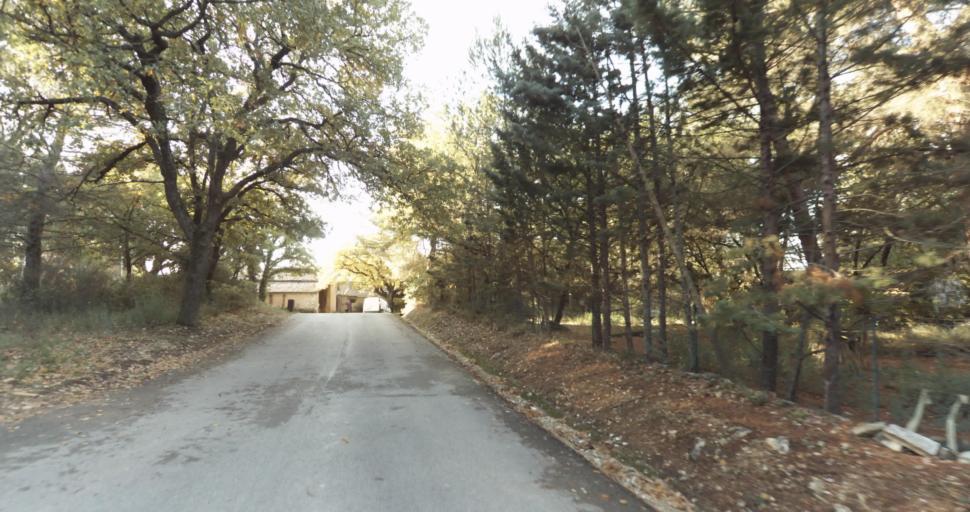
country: FR
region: Provence-Alpes-Cote d'Azur
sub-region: Departement des Bouches-du-Rhone
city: Venelles
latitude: 43.6012
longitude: 5.4745
